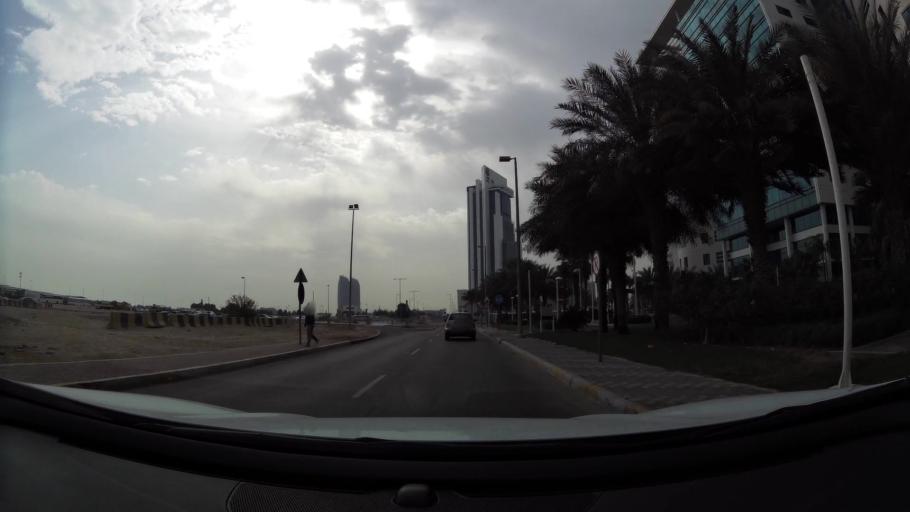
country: AE
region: Abu Dhabi
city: Abu Dhabi
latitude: 24.4641
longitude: 54.3885
